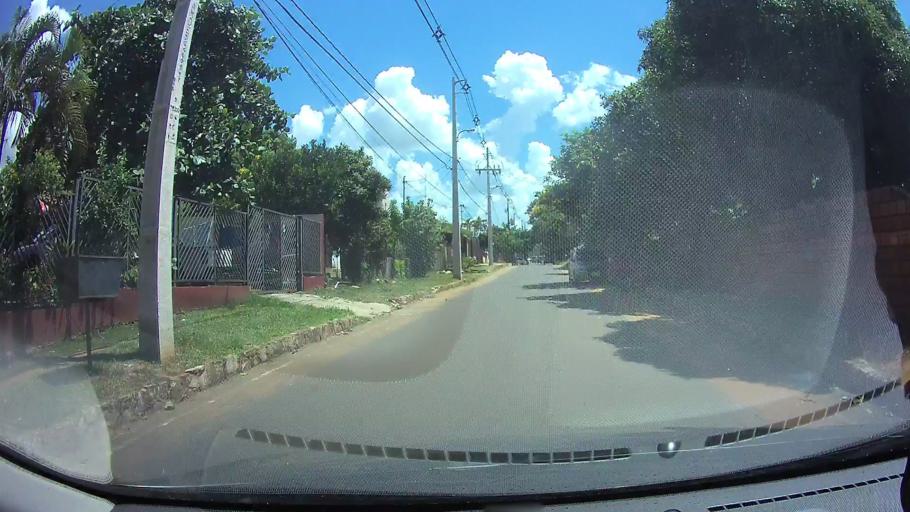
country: PY
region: Central
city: Limpio
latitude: -25.1524
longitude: -57.4521
